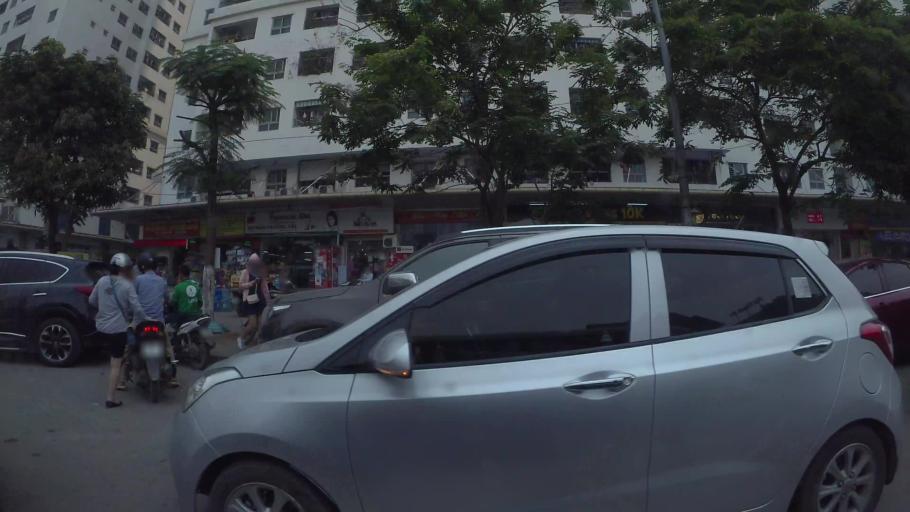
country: VN
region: Ha Noi
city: Van Dien
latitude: 20.9636
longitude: 105.8259
